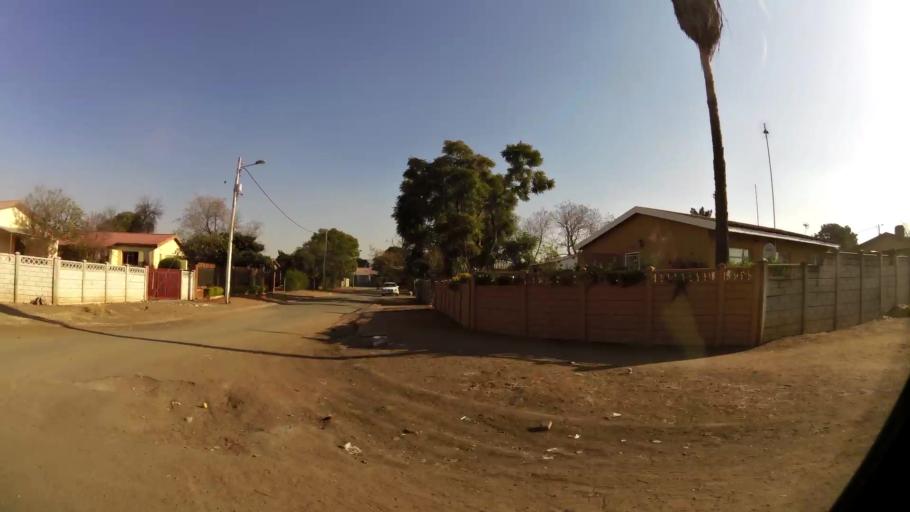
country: ZA
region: North-West
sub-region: Bojanala Platinum District Municipality
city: Rustenburg
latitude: -25.6427
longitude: 27.2395
